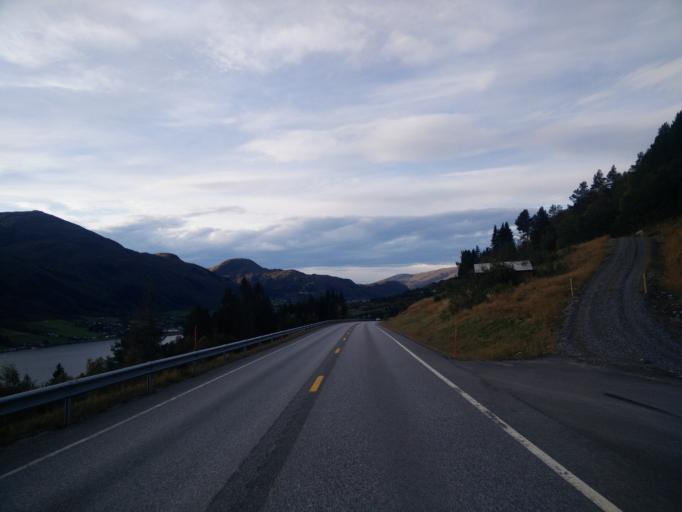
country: NO
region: More og Romsdal
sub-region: Gjemnes
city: Batnfjordsora
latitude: 62.9098
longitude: 7.6846
